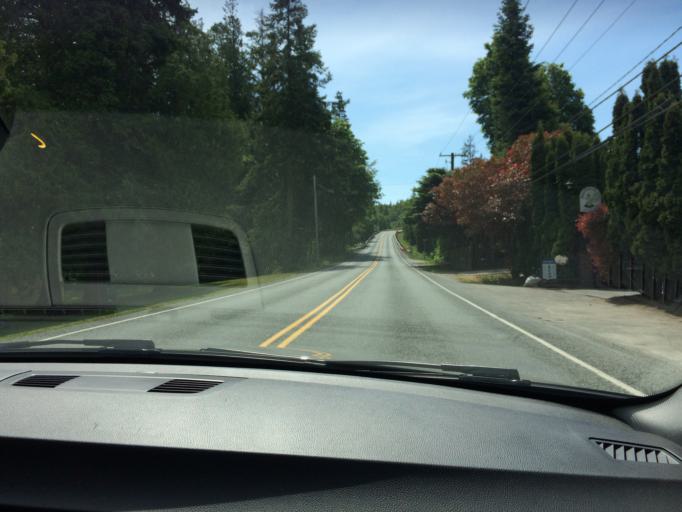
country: US
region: Washington
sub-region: Skagit County
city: Anacortes
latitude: 48.4569
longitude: -122.6530
